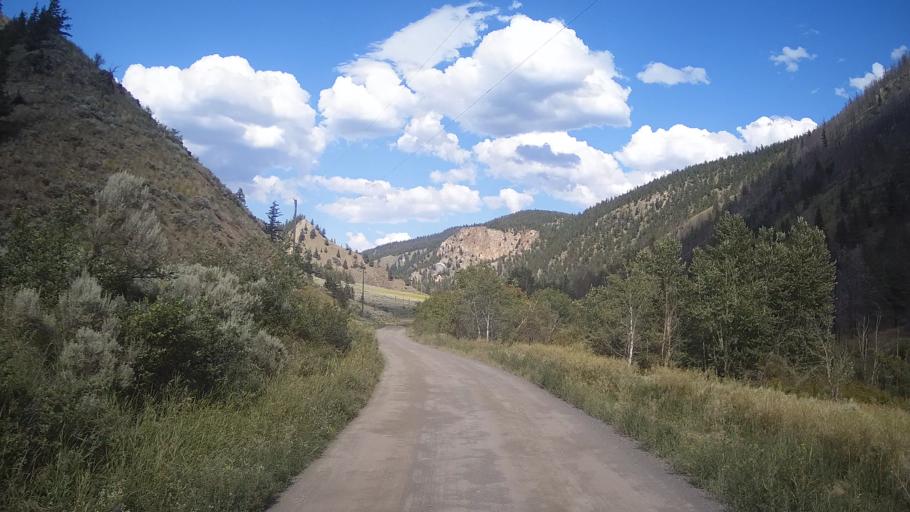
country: CA
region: British Columbia
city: Lillooet
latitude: 51.2199
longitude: -122.0779
